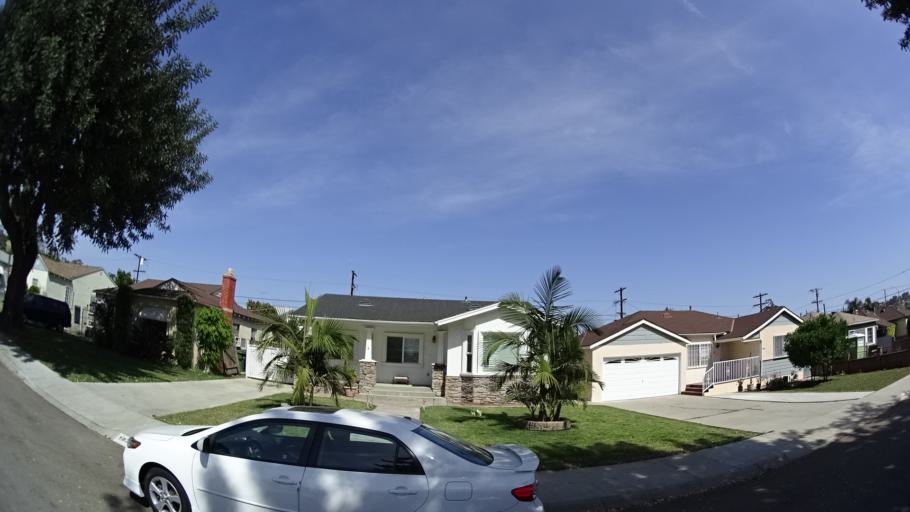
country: US
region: California
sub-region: Los Angeles County
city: Belvedere
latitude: 34.0642
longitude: -118.1891
